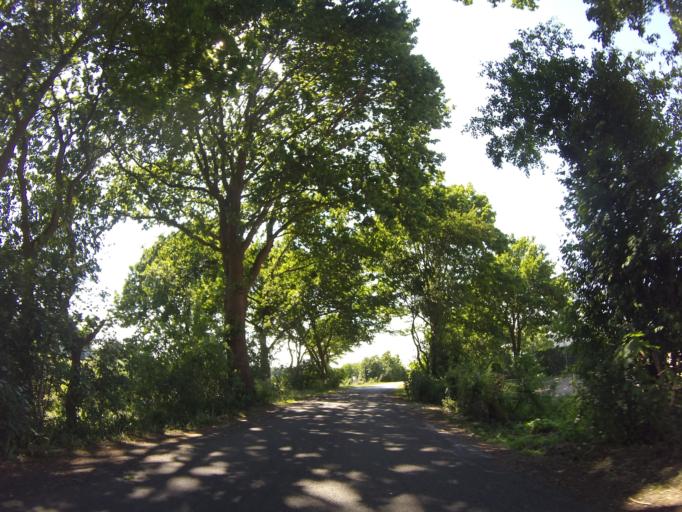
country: DE
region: Lower Saxony
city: Emlichheim
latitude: 52.6024
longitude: 6.8550
